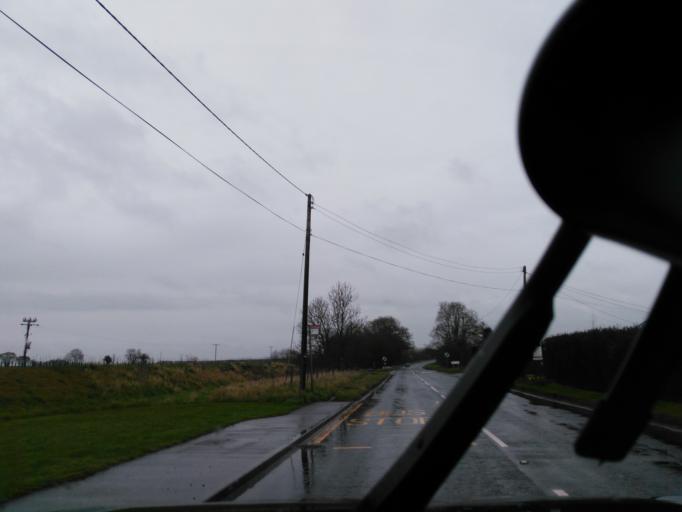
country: GB
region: England
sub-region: Wiltshire
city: Holt
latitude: 51.3337
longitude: -2.1684
